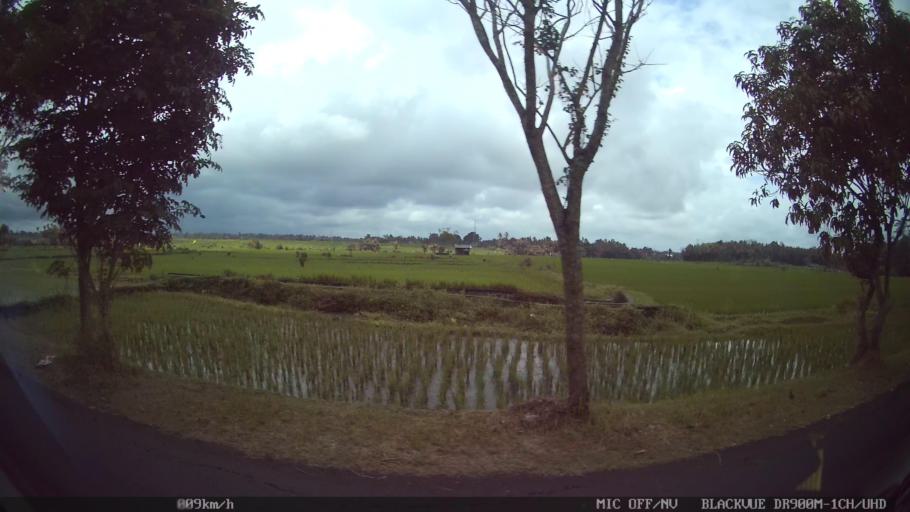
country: ID
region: Bali
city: Banjar Serangan
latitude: -8.5383
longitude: 115.1775
